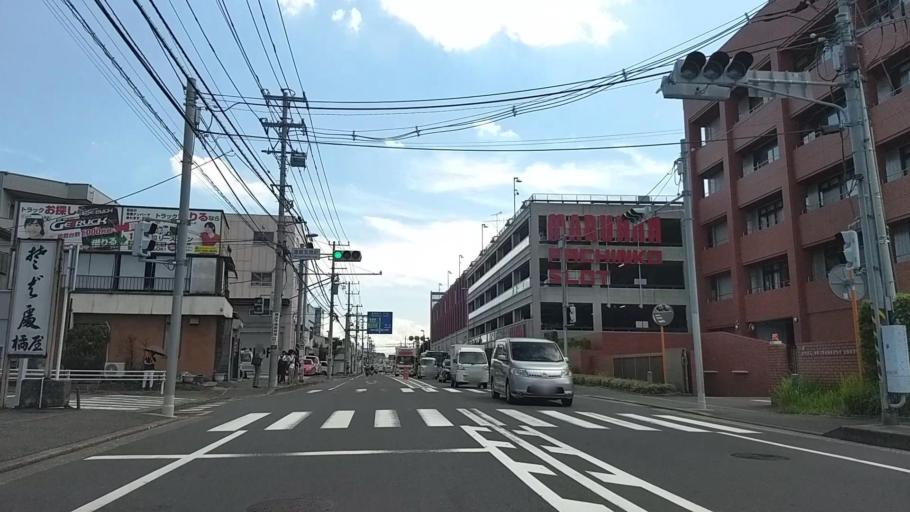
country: JP
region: Kanagawa
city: Yokohama
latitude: 35.5187
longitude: 139.5737
